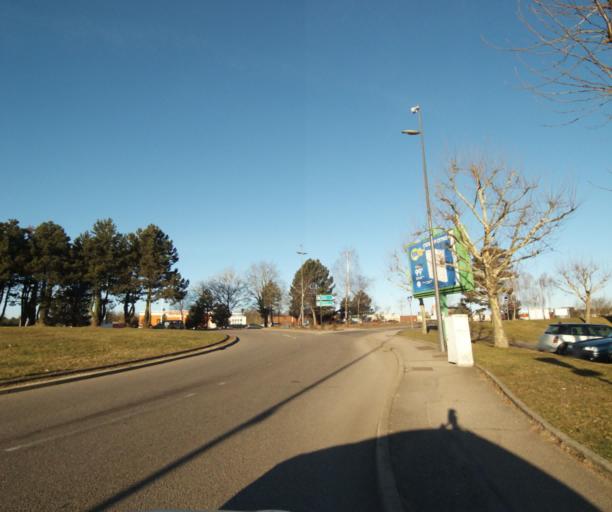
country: FR
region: Lorraine
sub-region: Departement de Meurthe-et-Moselle
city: Laxou
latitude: 48.6906
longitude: 6.1291
